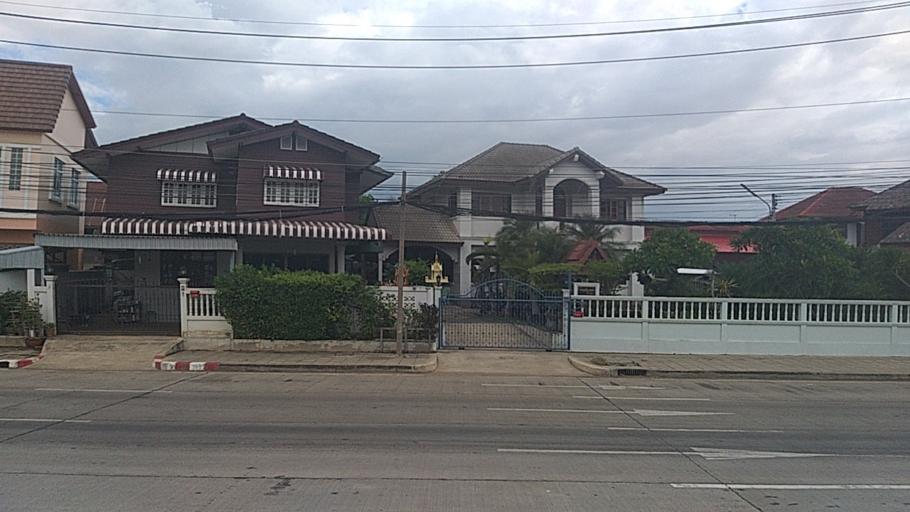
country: TH
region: Buriram
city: Prakhon Chai
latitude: 14.6097
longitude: 103.0833
